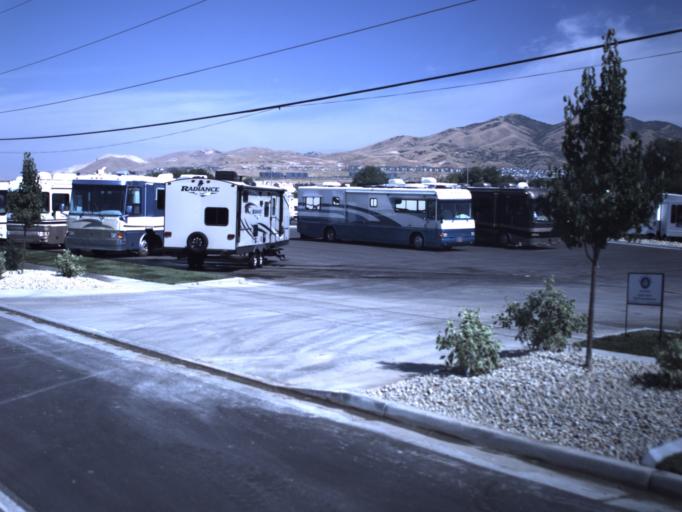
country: US
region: Utah
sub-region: Utah County
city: Lehi
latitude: 40.4099
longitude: -111.8651
